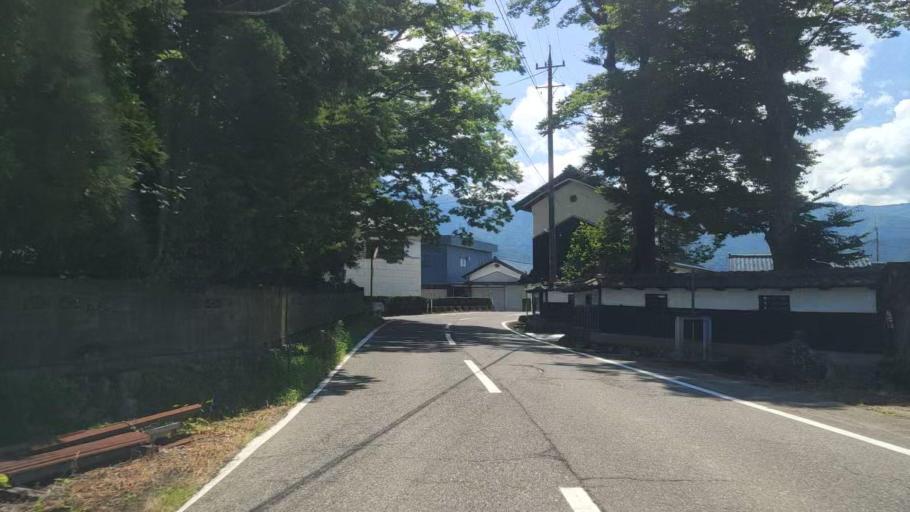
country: JP
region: Fukui
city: Ono
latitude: 35.9611
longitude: 136.5317
